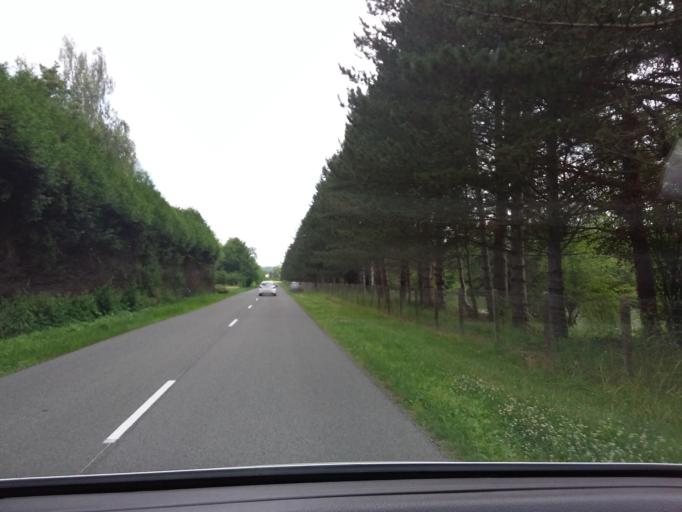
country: FR
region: Champagne-Ardenne
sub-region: Departement de la Marne
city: Fismes
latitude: 49.3821
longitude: 3.6498
